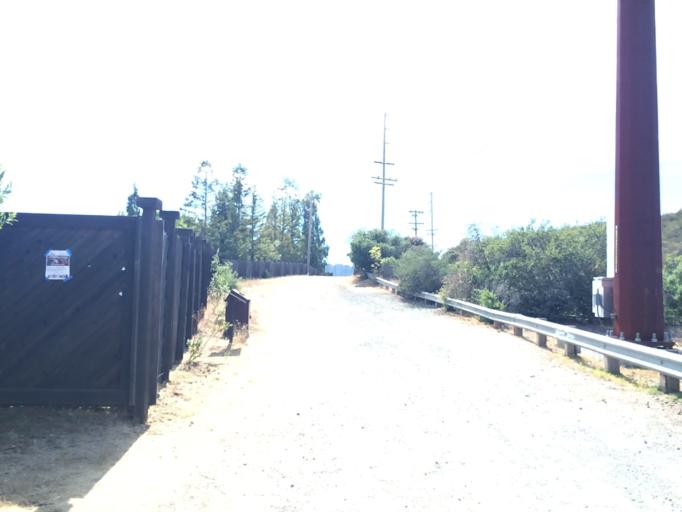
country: US
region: California
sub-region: San Mateo County
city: Emerald Lake Hills
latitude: 37.4619
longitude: -122.2760
